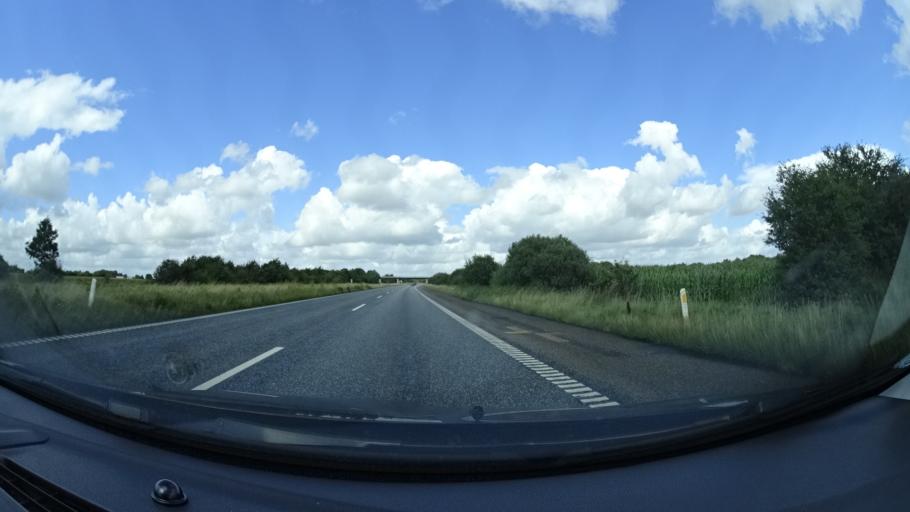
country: DK
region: South Denmark
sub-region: Aabenraa Kommune
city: Krusa
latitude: 54.8982
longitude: 9.3774
